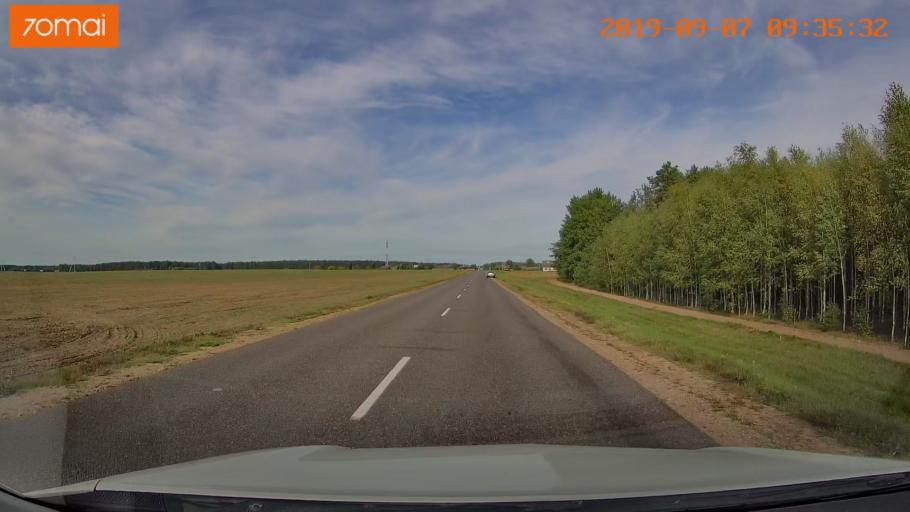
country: BY
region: Grodnenskaya
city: Iwye
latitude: 53.9116
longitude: 25.8683
